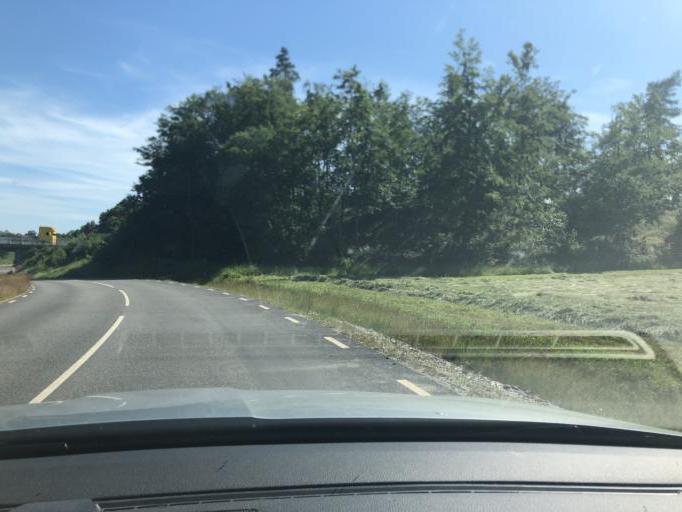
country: SE
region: Blekinge
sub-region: Karlshamns Kommun
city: Morrum
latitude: 56.1767
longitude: 14.7022
